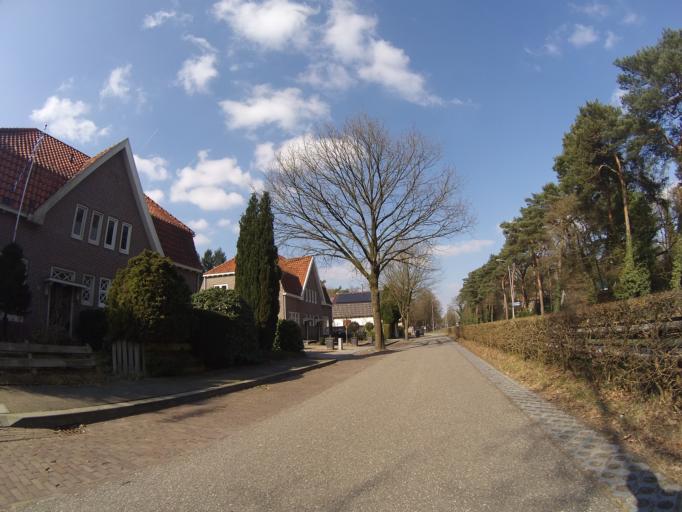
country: NL
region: Utrecht
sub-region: Gemeente Zeist
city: Zeist
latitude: 52.1461
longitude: 5.2378
